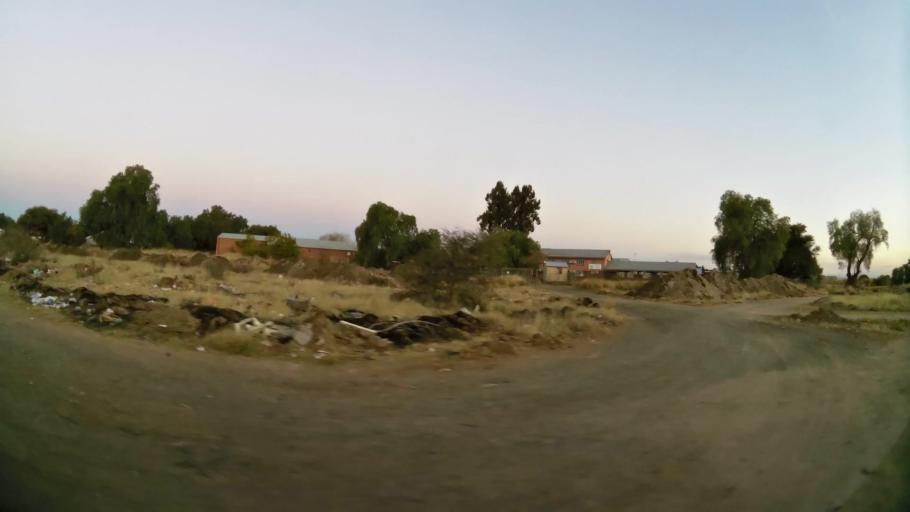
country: ZA
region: Northern Cape
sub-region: Frances Baard District Municipality
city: Kimberley
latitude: -28.7235
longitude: 24.7647
